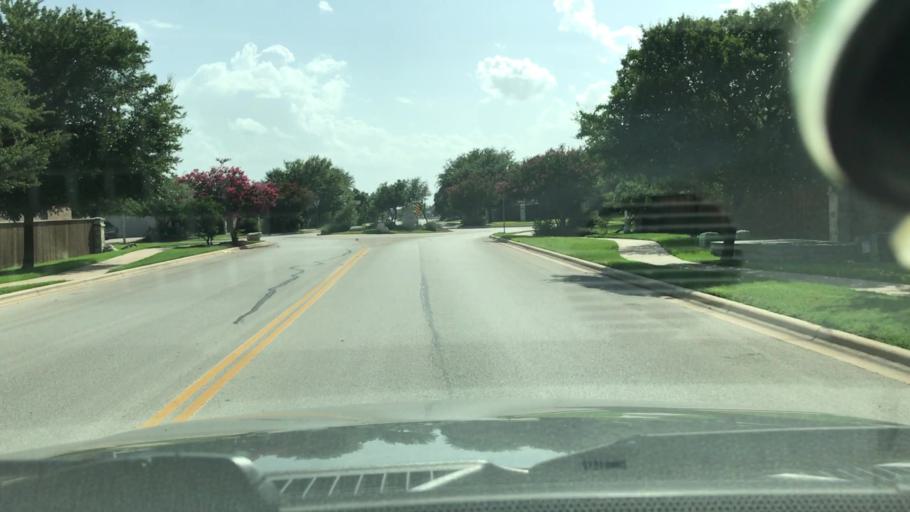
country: US
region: Texas
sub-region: Williamson County
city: Leander
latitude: 30.5397
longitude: -97.8568
